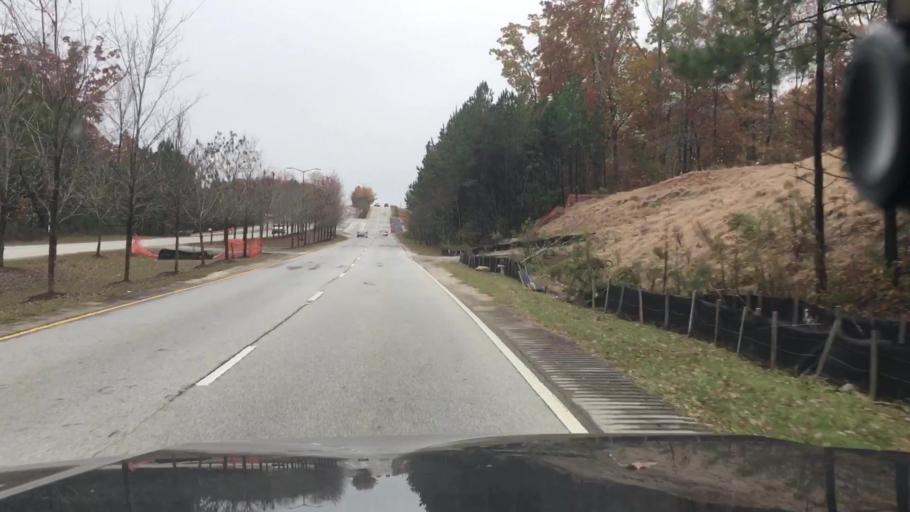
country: US
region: Georgia
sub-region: Coweta County
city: East Newnan
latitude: 33.3844
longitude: -84.7532
